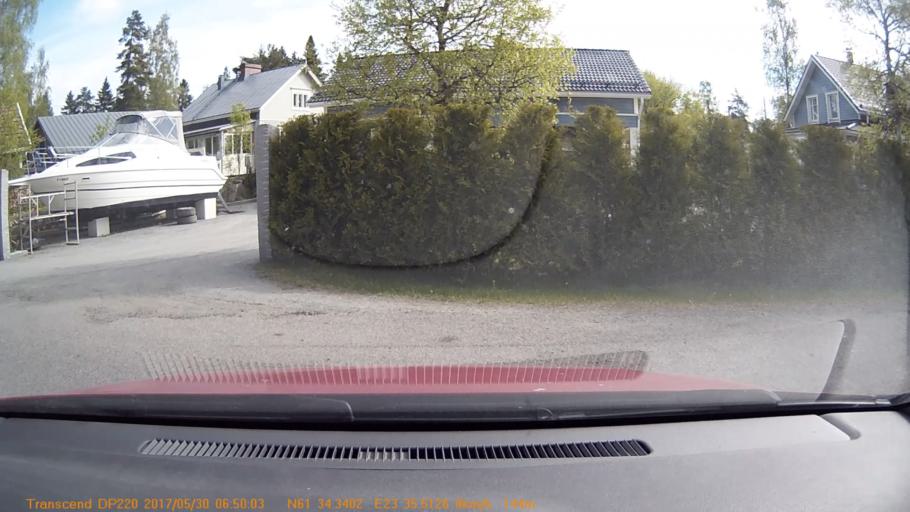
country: FI
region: Pirkanmaa
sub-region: Tampere
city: Yloejaervi
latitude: 61.5723
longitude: 23.5919
